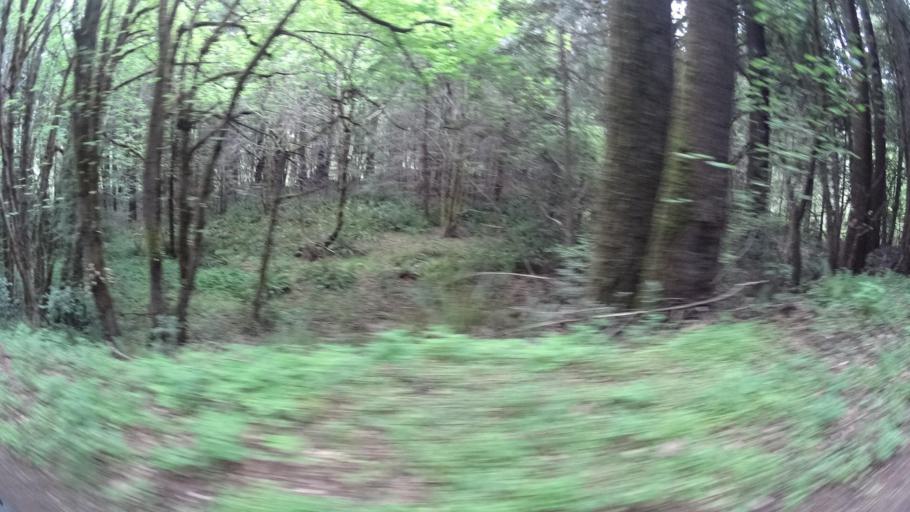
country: US
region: California
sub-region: Humboldt County
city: Blue Lake
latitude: 40.9599
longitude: -123.8380
